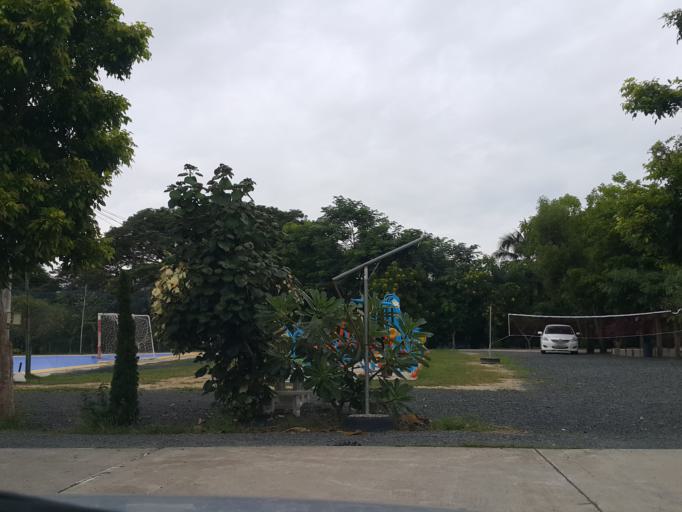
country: TH
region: Chiang Mai
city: San Kamphaeng
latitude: 18.8124
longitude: 99.1262
